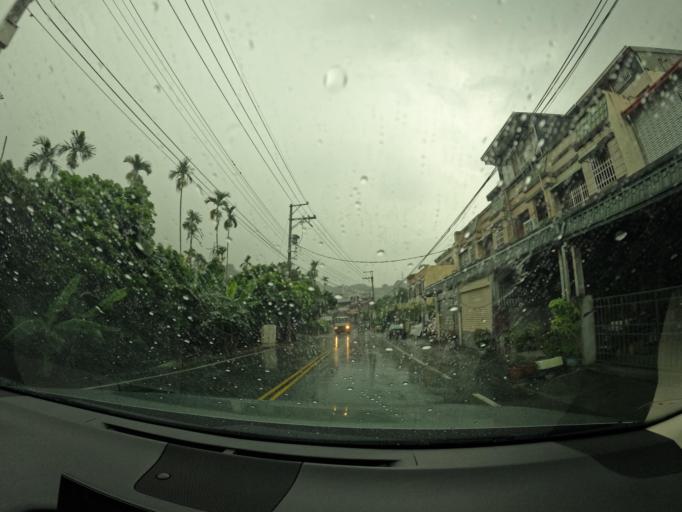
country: TW
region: Taiwan
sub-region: Nantou
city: Nantou
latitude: 23.8880
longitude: 120.7388
